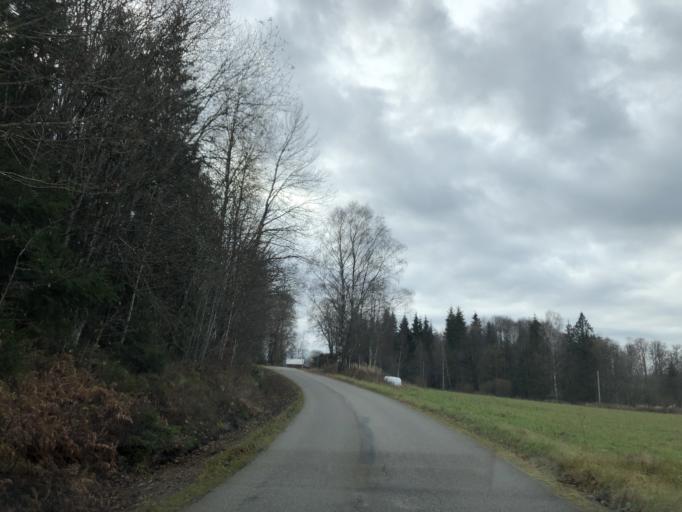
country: SE
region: Vaestra Goetaland
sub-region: Ulricehamns Kommun
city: Ulricehamn
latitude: 57.7246
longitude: 13.3588
